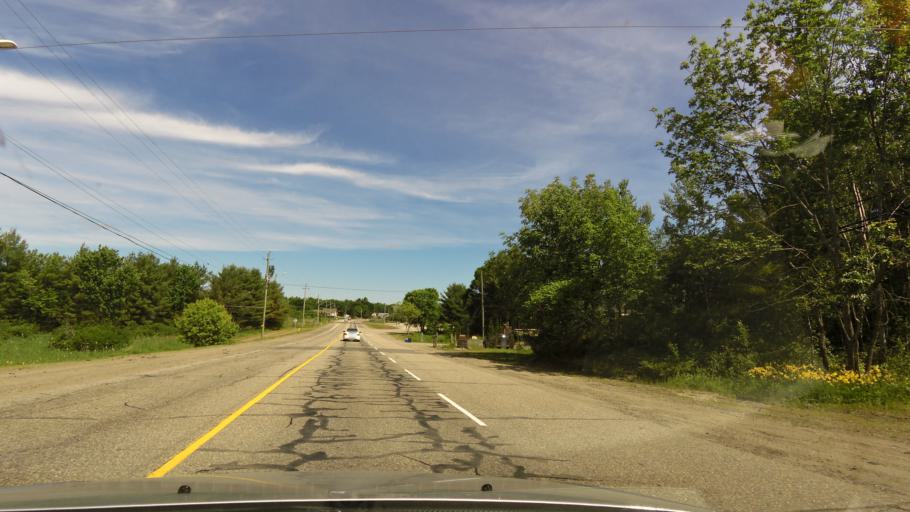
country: CA
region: Ontario
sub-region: Parry Sound District
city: Parry Sound
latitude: 45.3649
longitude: -80.0435
